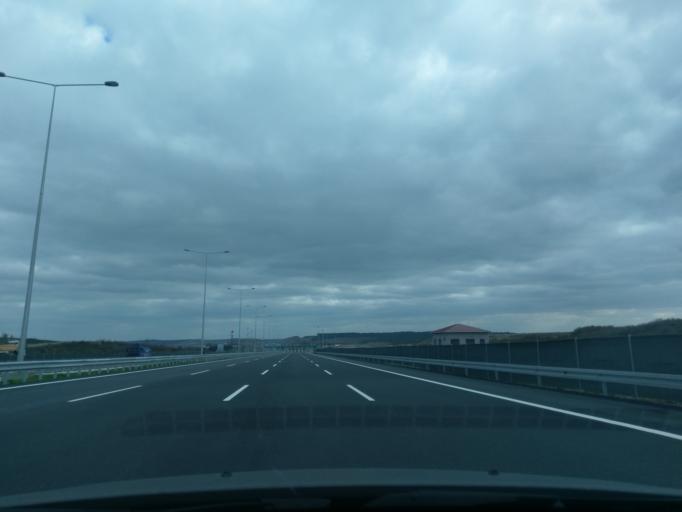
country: TR
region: Istanbul
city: Durusu
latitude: 41.2440
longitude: 28.7047
